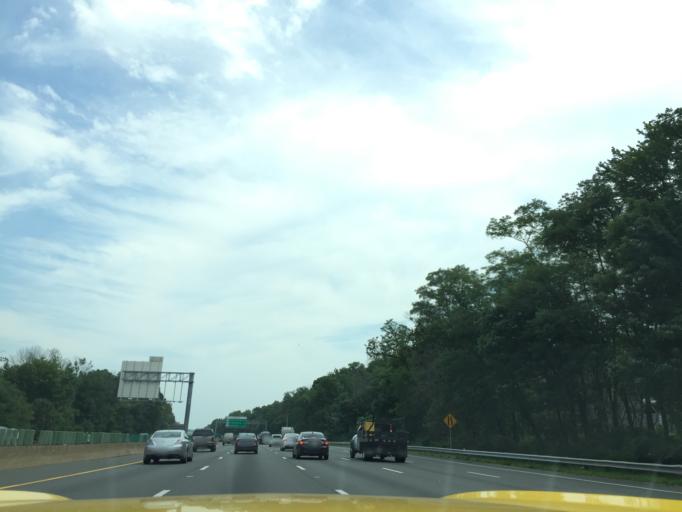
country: US
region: Virginia
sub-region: Fairfax County
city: Rose Hill
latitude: 38.7971
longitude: -77.1302
